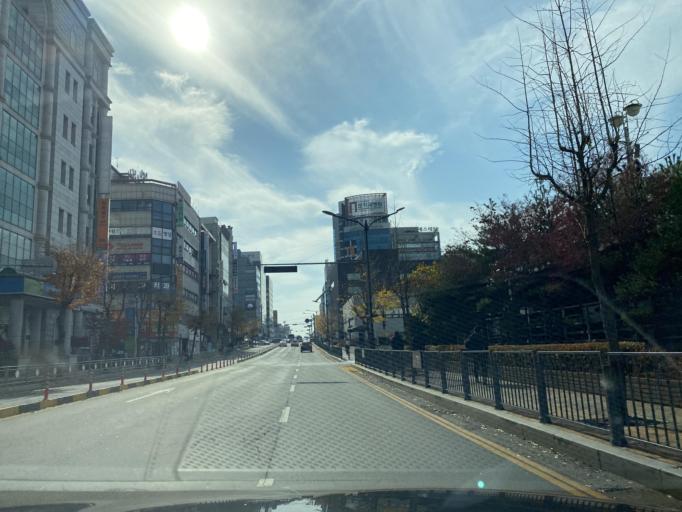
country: KR
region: Chungcheongnam-do
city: Cheonan
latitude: 36.8207
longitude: 127.1582
